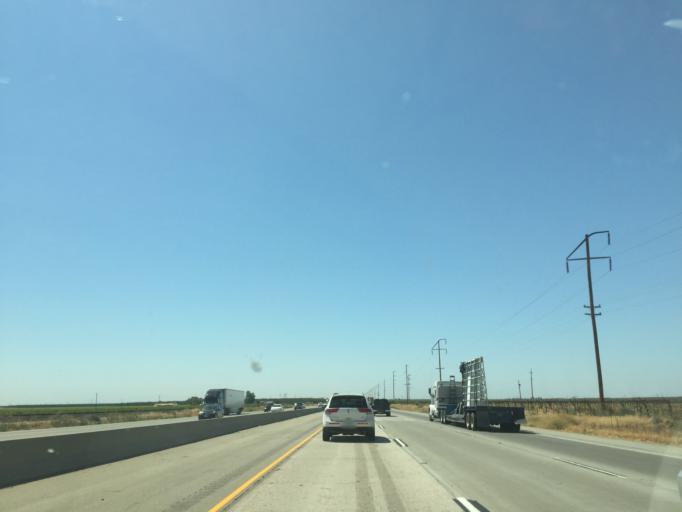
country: US
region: California
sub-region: Kern County
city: Greenacres
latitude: 35.4680
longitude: -119.1222
